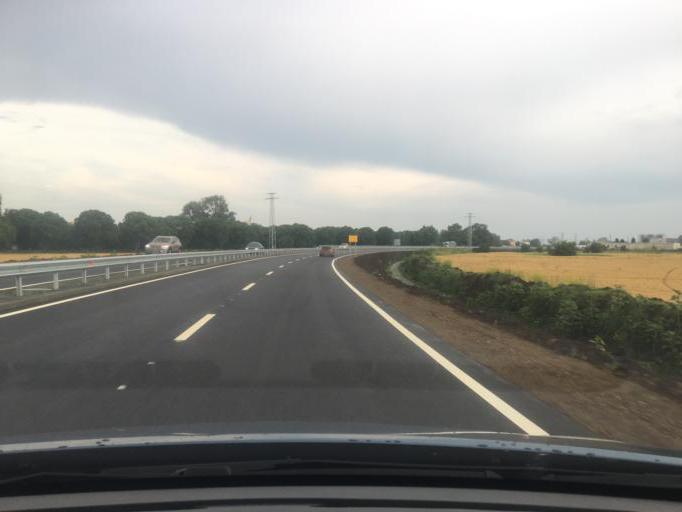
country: BG
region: Burgas
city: Aheloy
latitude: 42.6411
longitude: 27.6387
